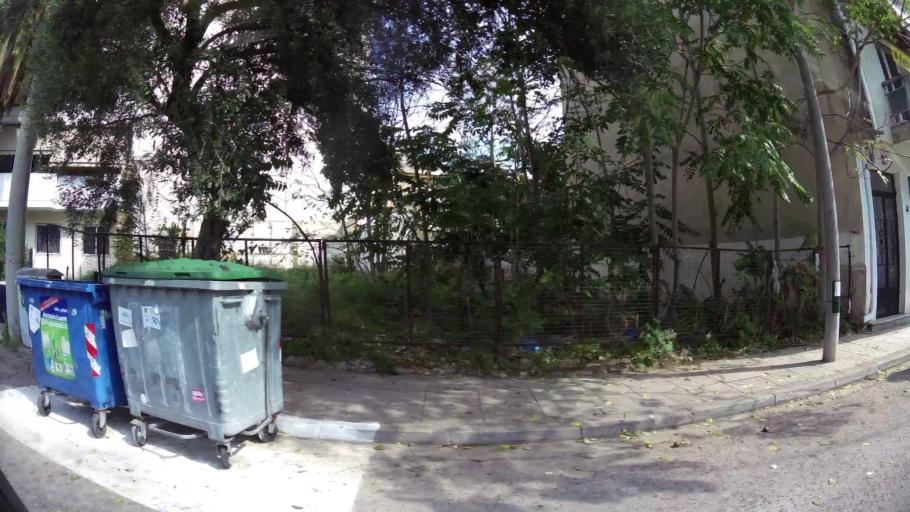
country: GR
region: Attica
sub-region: Nomarchia Athinas
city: Athens
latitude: 37.9947
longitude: 23.7085
